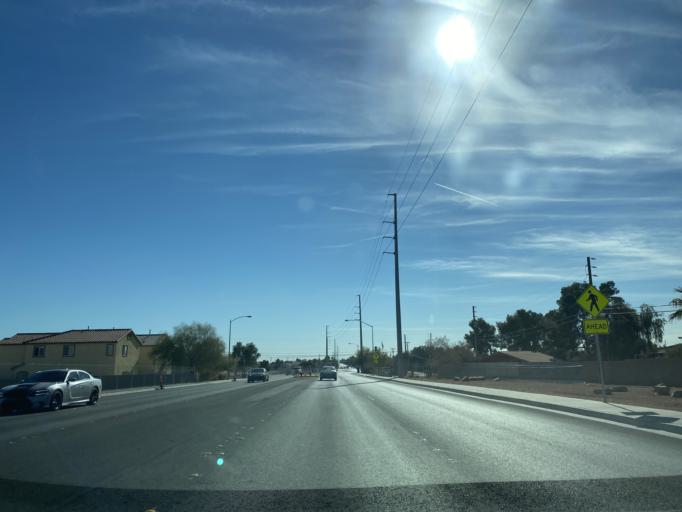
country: US
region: Nevada
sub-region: Clark County
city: North Las Vegas
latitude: 36.2447
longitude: -115.1437
